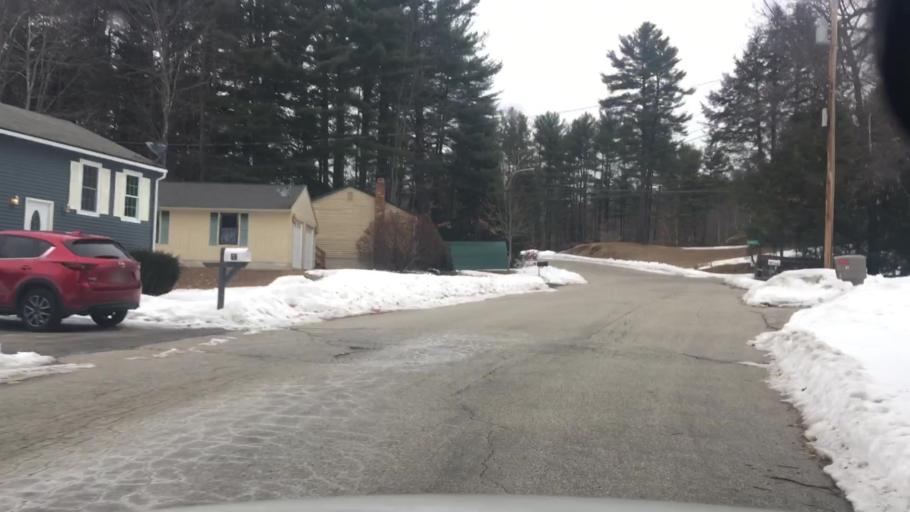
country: US
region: Maine
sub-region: York County
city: Springvale
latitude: 43.4710
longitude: -70.7907
